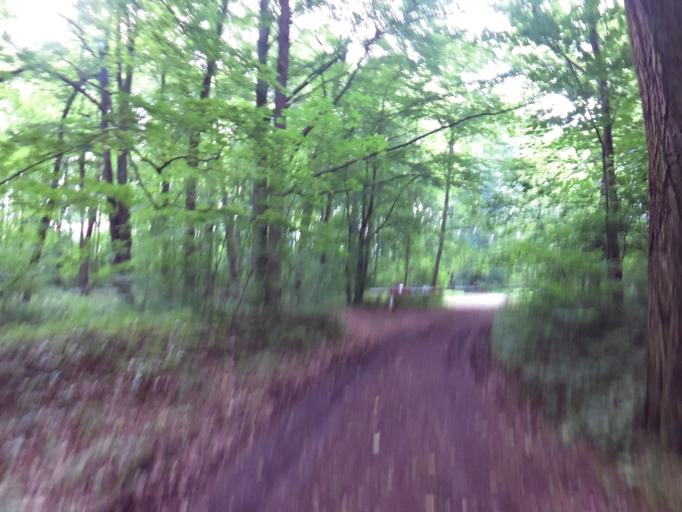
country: CZ
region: Ustecky
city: Dolni Podluzi
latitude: 50.8925
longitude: 14.6086
